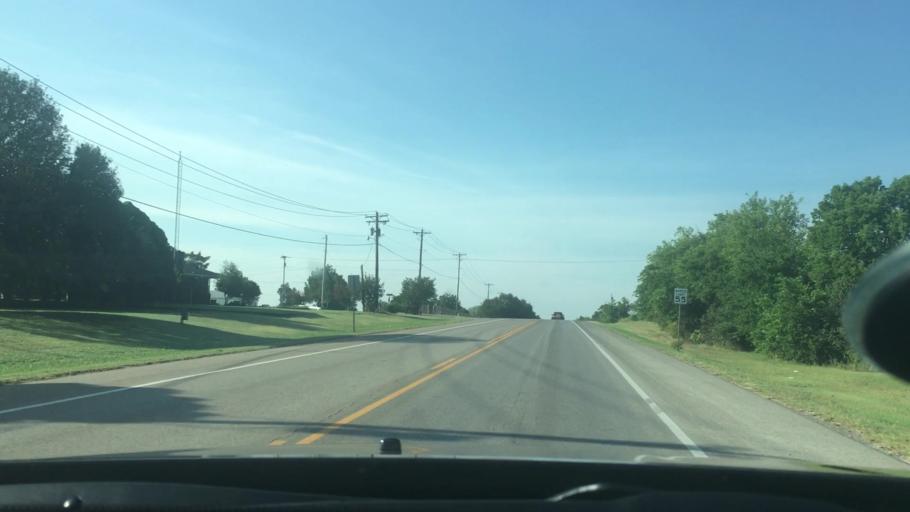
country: US
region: Oklahoma
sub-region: Garvin County
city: Pauls Valley
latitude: 34.7163
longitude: -97.2130
